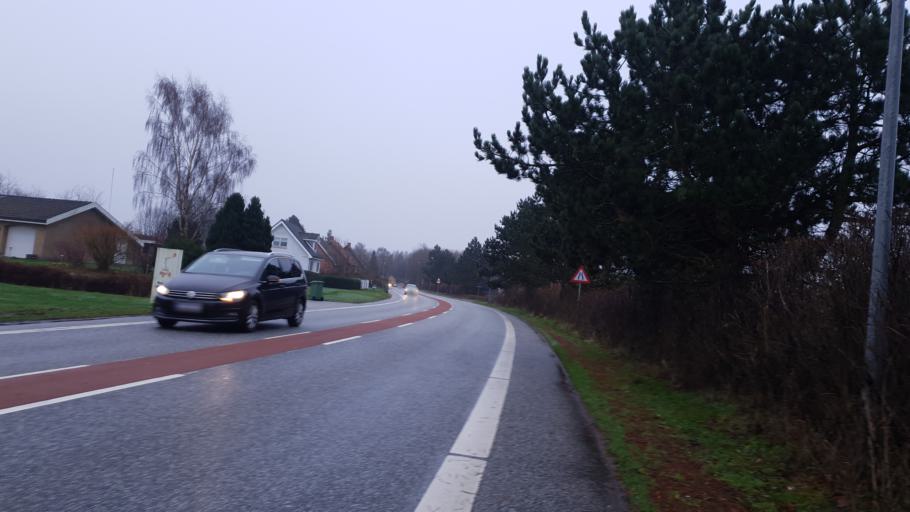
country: DK
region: Central Jutland
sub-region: Hedensted Kommune
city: Hedensted
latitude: 55.7768
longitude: 9.6961
